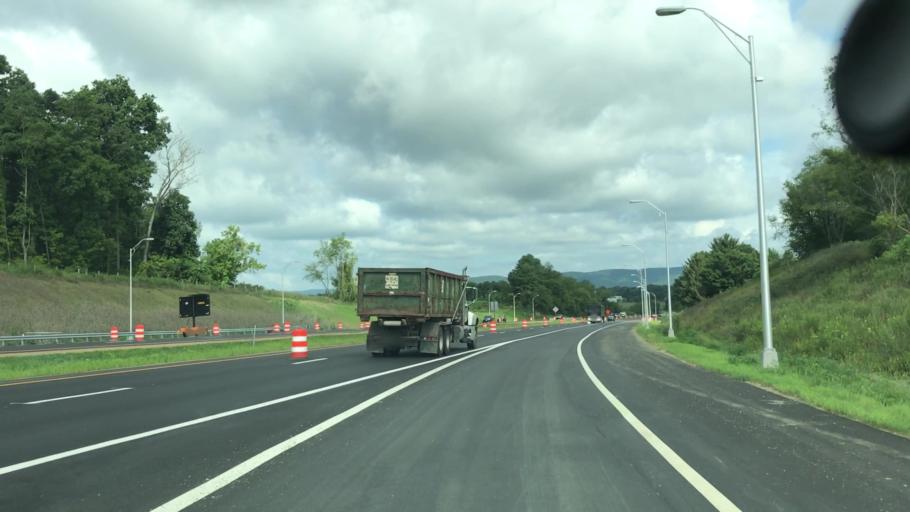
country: US
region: Virginia
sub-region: Montgomery County
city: Merrimac
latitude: 37.2113
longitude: -80.4297
